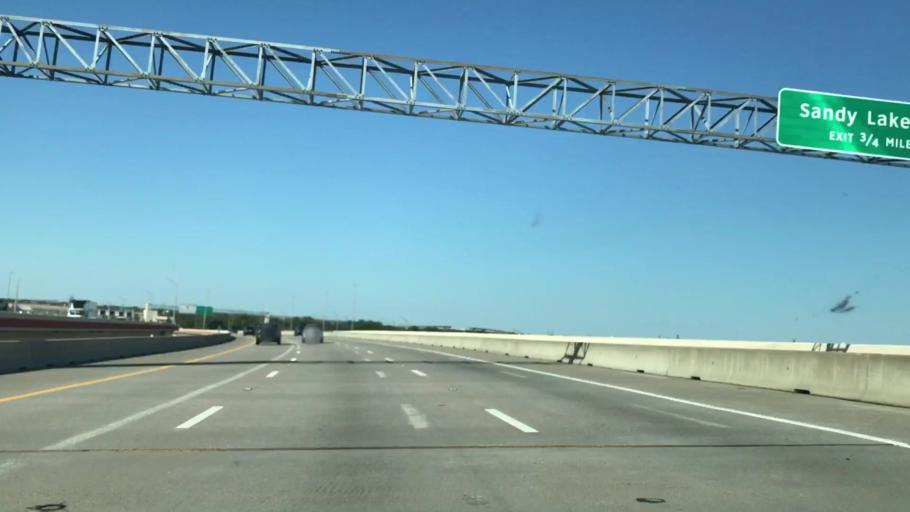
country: US
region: Texas
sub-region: Dallas County
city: Carrollton
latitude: 32.9541
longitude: -96.9257
